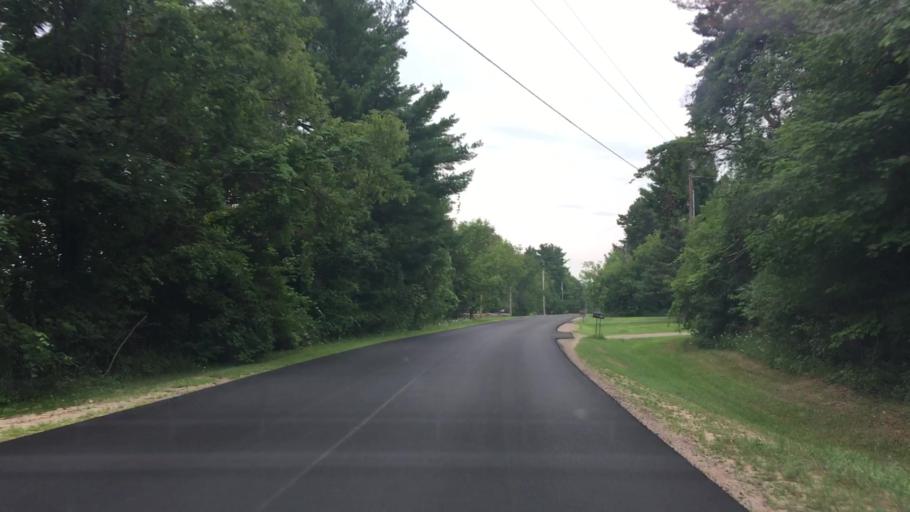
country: US
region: New York
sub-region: Clinton County
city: Peru
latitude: 44.5615
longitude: -73.5674
